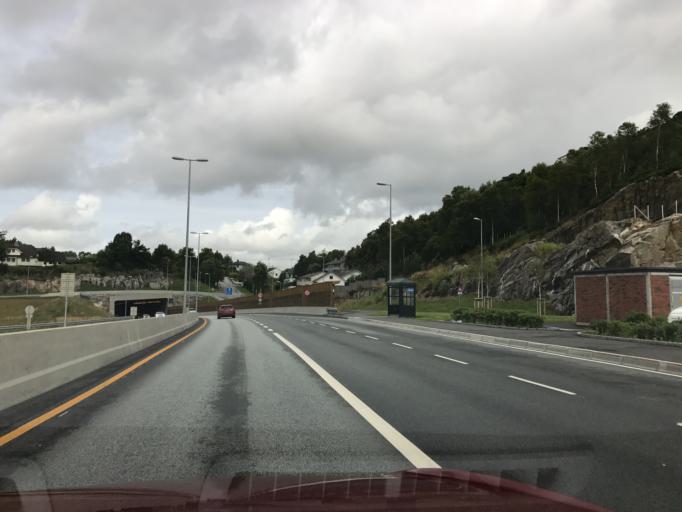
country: NO
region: Rogaland
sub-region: Karmoy
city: Eike
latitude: 59.4221
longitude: 5.3931
